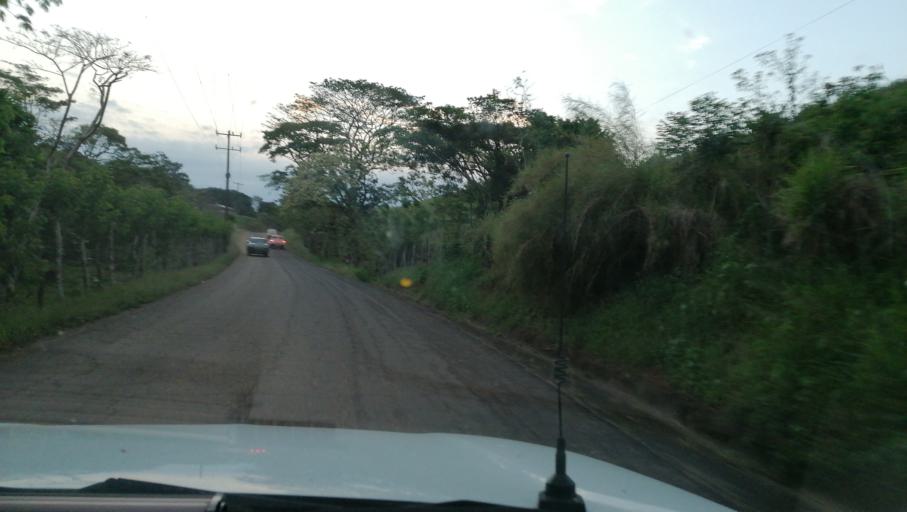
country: MX
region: Chiapas
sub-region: Ostuacan
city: Nuevo Juan del Grijalva
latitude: 17.4466
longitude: -93.3560
